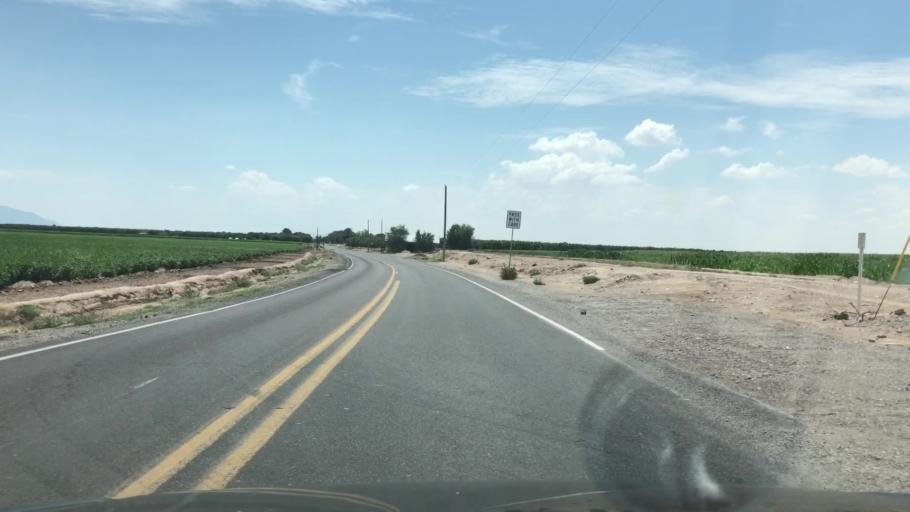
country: US
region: New Mexico
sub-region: Dona Ana County
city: Berino
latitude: 32.0263
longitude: -106.6720
